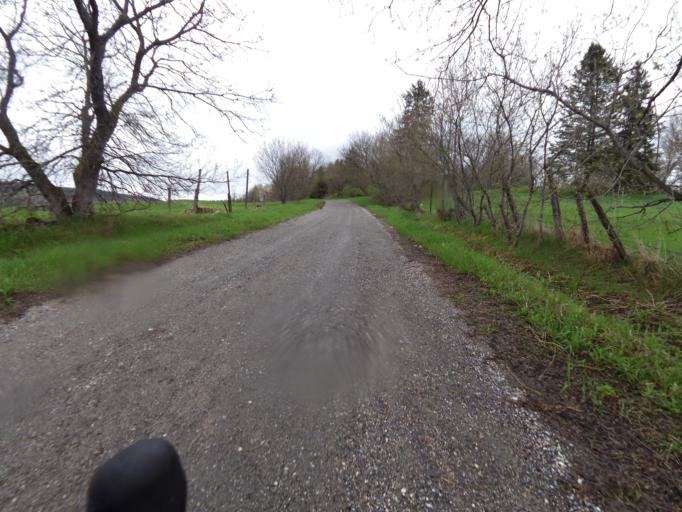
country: CA
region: Quebec
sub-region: Outaouais
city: Wakefield
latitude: 45.5804
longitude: -75.8916
